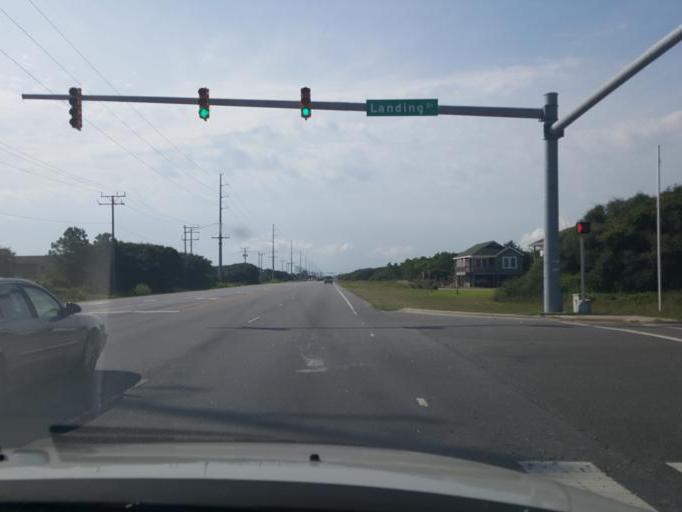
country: US
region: North Carolina
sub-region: Dare County
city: Kill Devil Hills
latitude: 36.0260
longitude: -75.6684
